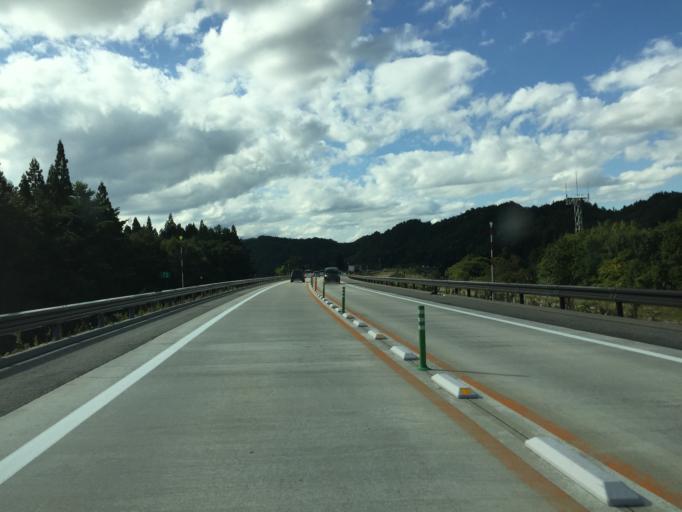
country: JP
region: Yamagata
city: Yonezawa
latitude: 37.8686
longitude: 140.2105
